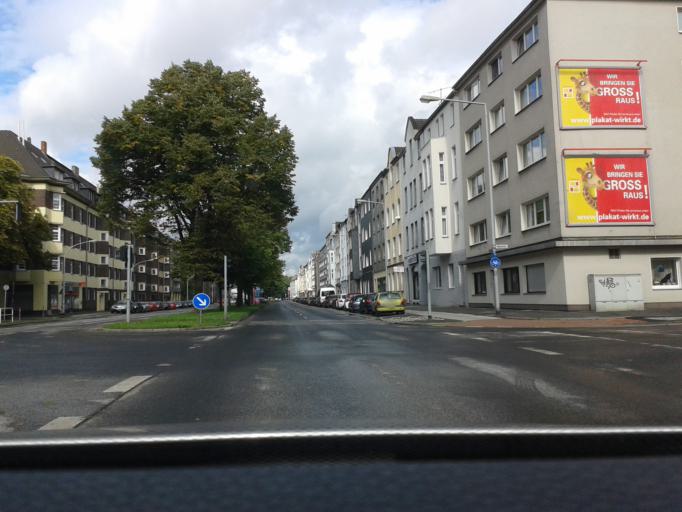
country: DE
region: North Rhine-Westphalia
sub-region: Regierungsbezirk Dusseldorf
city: Duisburg
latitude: 51.4169
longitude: 6.7907
